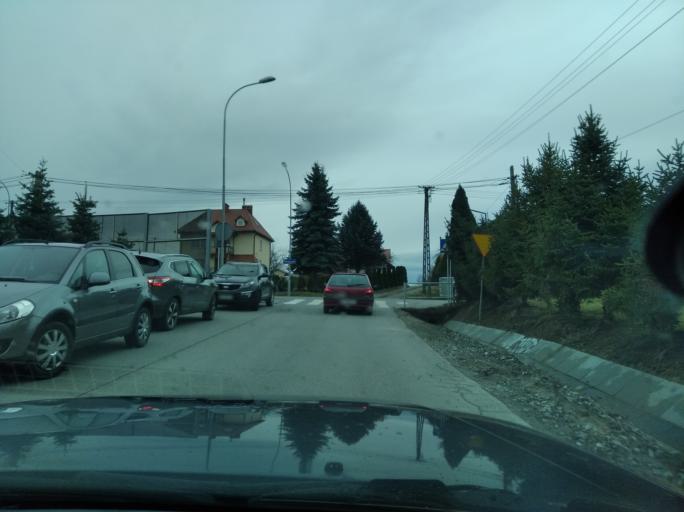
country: PL
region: Subcarpathian Voivodeship
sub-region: Powiat rzeszowski
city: Siedliska
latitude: 49.9694
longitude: 21.9872
